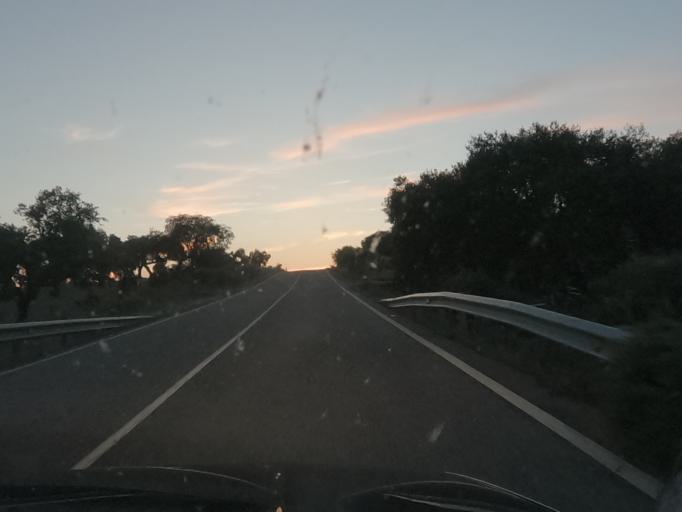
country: ES
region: Extremadura
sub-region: Provincia de Caceres
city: Piedras Albas
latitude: 39.7847
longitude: -6.9418
